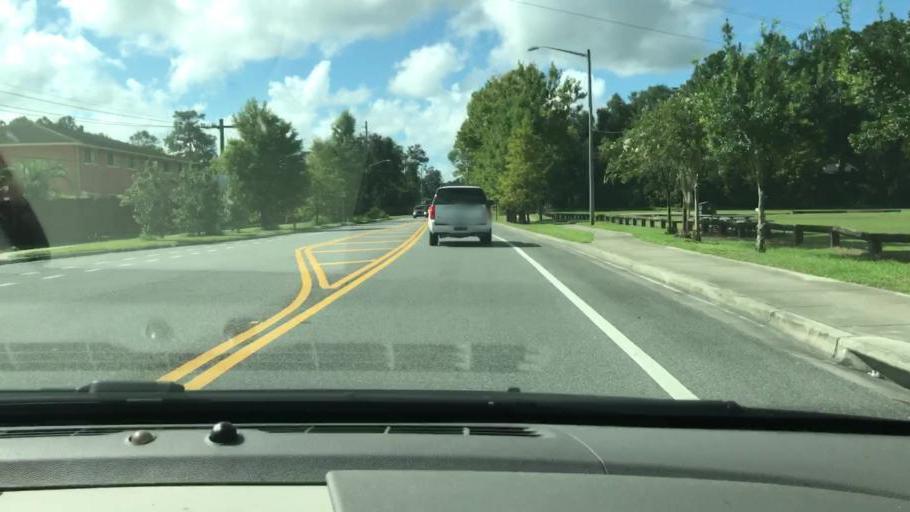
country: US
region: Florida
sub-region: Alachua County
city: Gainesville
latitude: 29.6352
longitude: -82.3893
